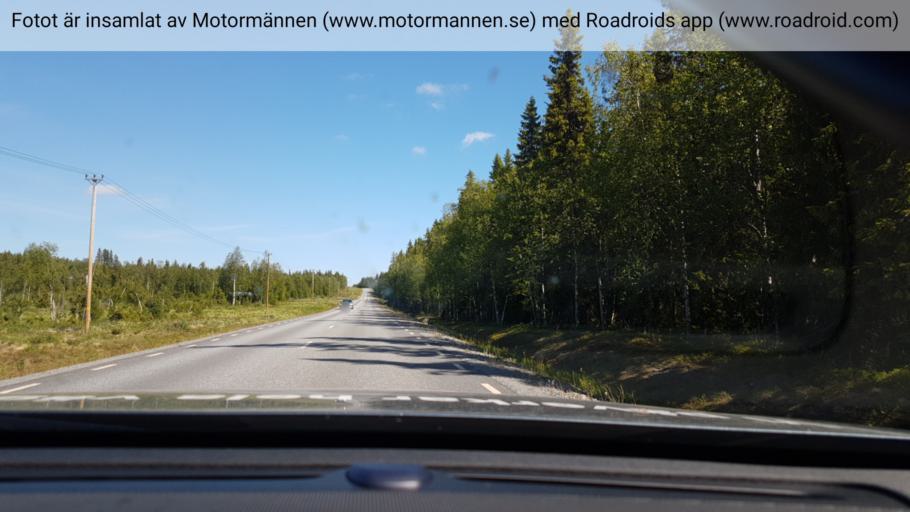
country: SE
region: Vaesterbotten
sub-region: Storumans Kommun
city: Storuman
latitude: 64.7040
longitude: 17.1419
